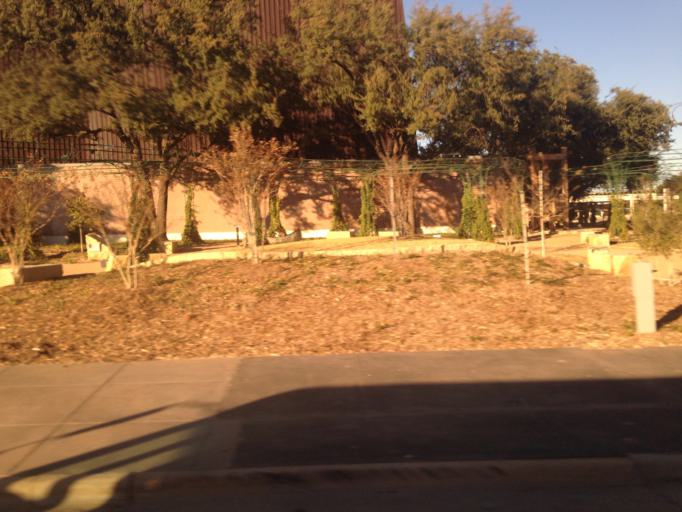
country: US
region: Texas
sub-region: Taylor County
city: Abilene
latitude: 32.4548
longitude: -99.7328
